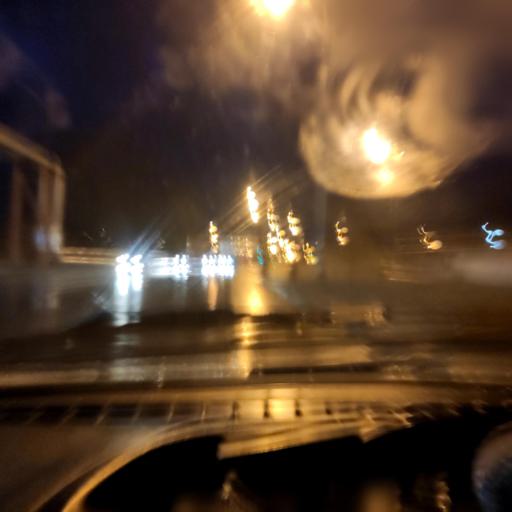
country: RU
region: Samara
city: Zhigulevsk
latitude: 53.4858
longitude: 49.5107
